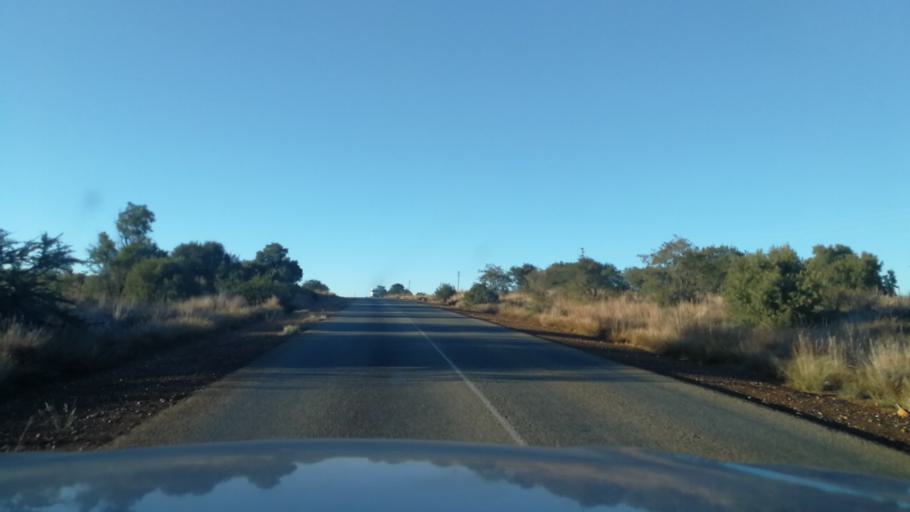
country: ZA
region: North-West
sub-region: Bojanala Platinum District Municipality
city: Koster
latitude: -25.7814
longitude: 26.7764
